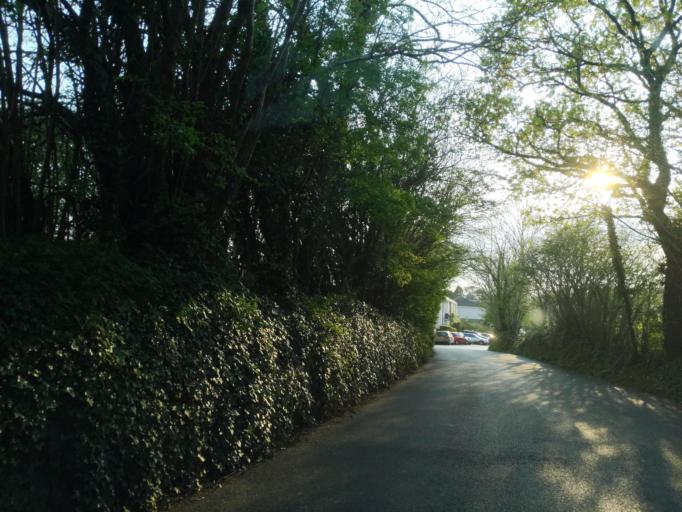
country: GB
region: England
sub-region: Devon
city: Plympton
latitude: 50.3622
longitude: -4.0512
